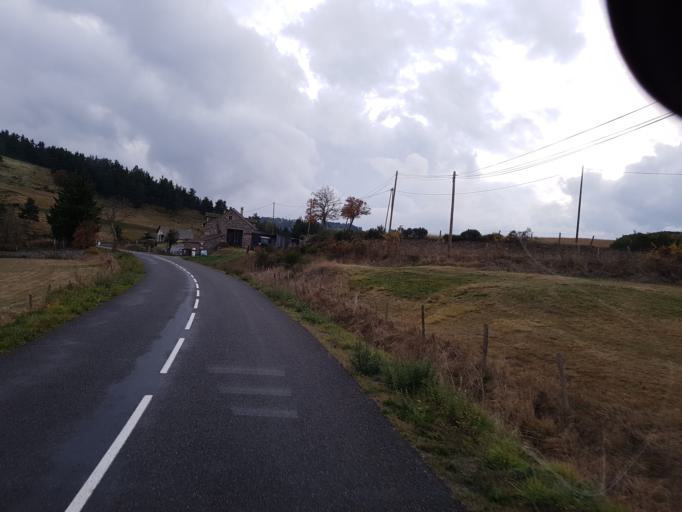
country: FR
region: Languedoc-Roussillon
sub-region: Departement de la Lozere
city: Langogne
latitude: 44.6566
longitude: 3.6910
